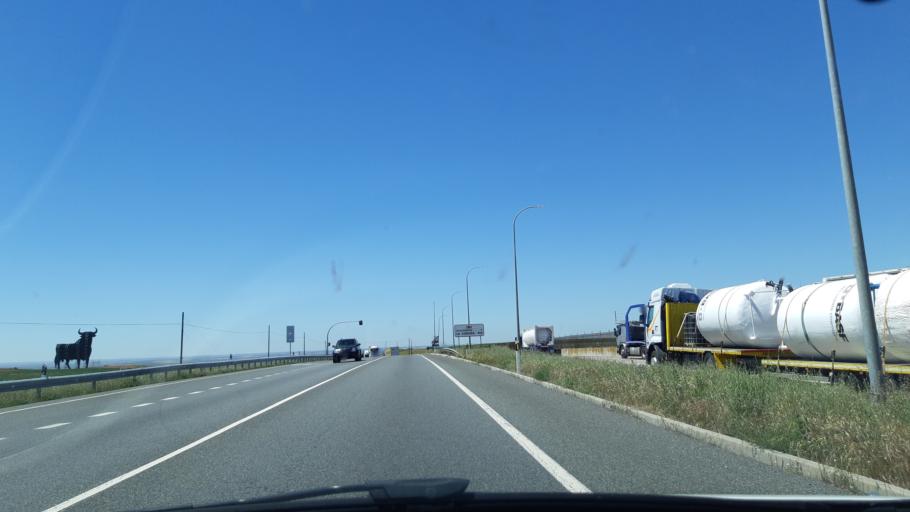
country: ES
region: Castille and Leon
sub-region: Provincia de Segovia
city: Labajos
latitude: 40.8428
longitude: -4.5231
